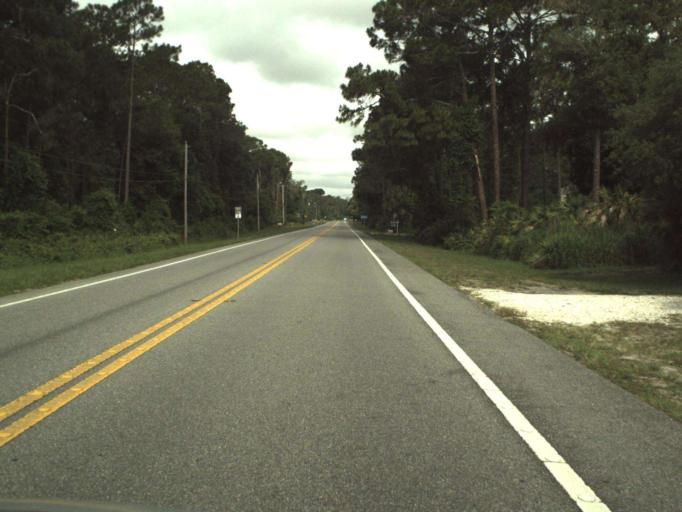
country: US
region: Florida
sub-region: Seminole County
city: Geneva
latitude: 28.7259
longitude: -81.0992
